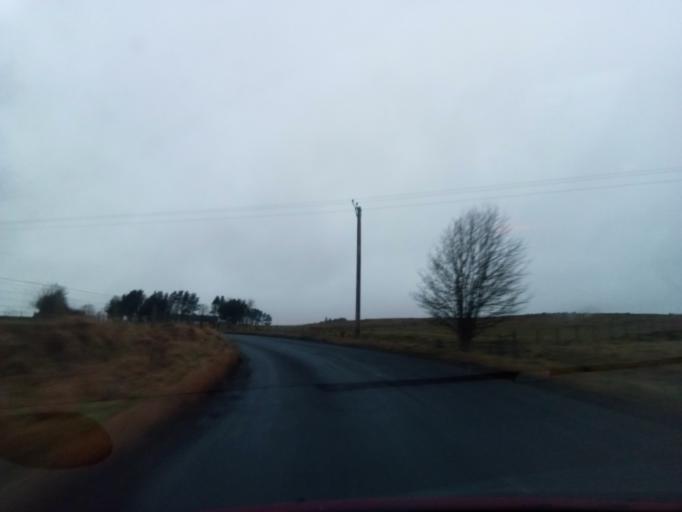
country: GB
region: England
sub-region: Northumberland
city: Otterburn
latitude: 55.2330
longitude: -2.1090
